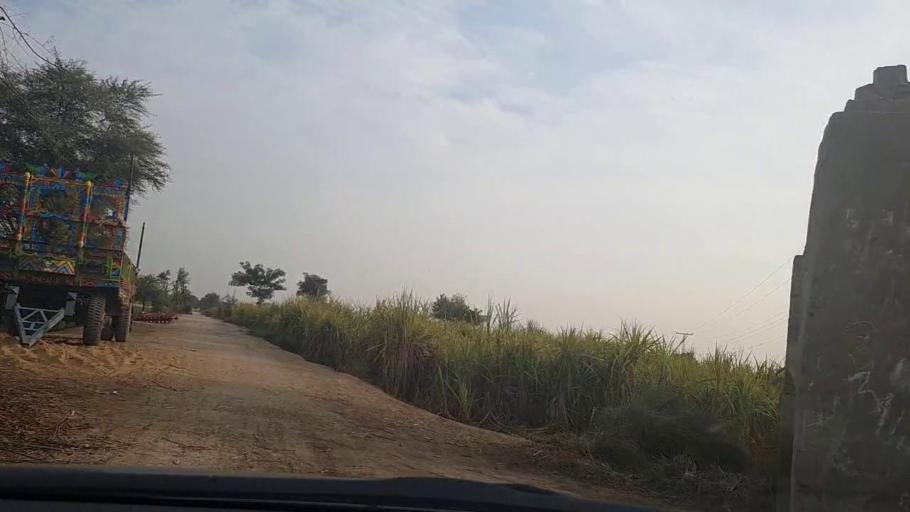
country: PK
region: Sindh
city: Daulatpur
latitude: 26.3305
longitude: 68.0246
